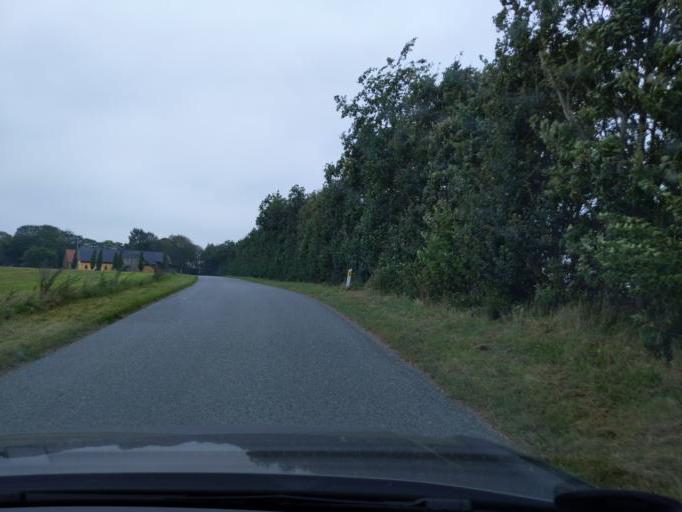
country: DK
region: Central Jutland
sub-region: Viborg Kommune
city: Viborg
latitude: 56.4969
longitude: 9.3204
